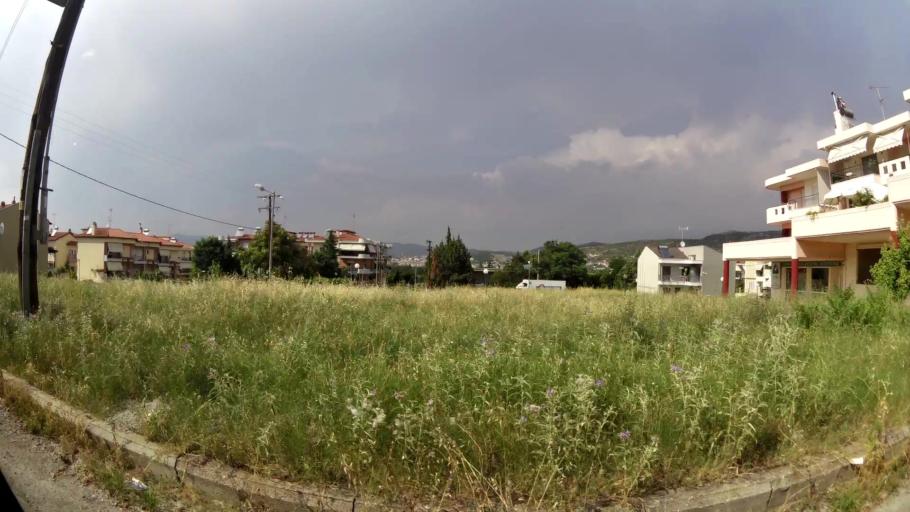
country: GR
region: Central Macedonia
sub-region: Nomos Thessalonikis
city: Polichni
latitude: 40.6679
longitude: 22.9511
